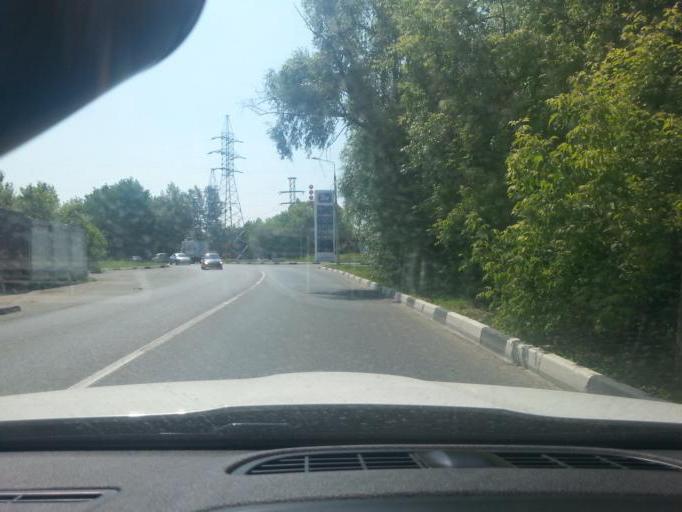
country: RU
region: Moskovskaya
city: Zheleznodorozhnyy
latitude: 55.7336
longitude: 38.0101
